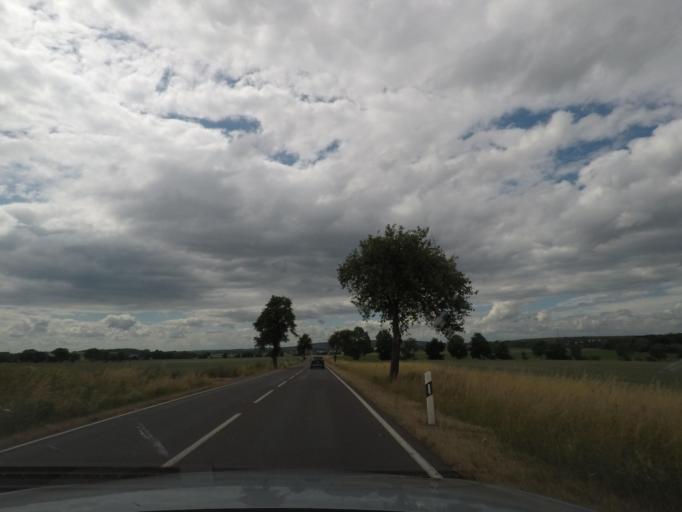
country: DE
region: Saxony-Anhalt
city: Hotensleben
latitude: 52.1061
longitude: 11.0419
